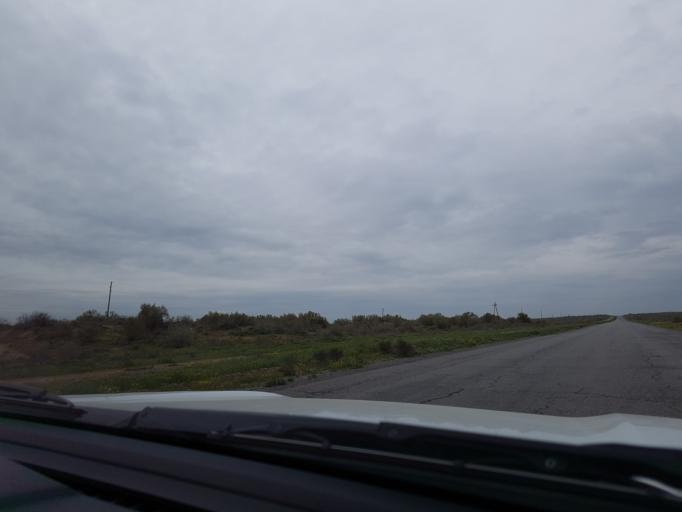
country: TM
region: Mary
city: Bayramaly
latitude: 37.8475
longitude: 62.5909
